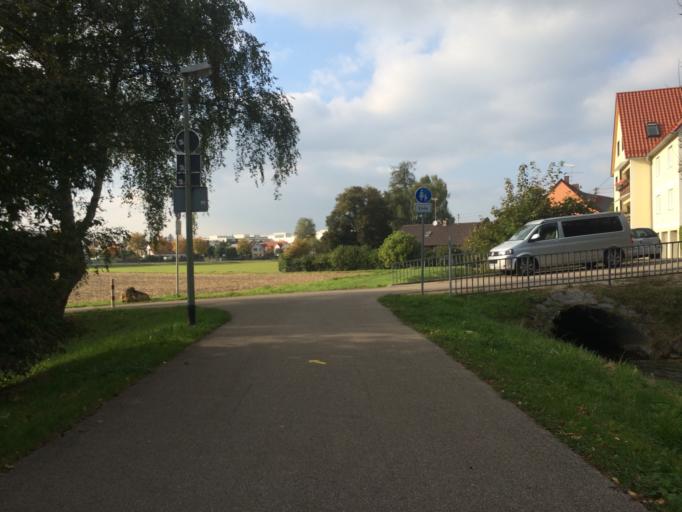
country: DE
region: Bavaria
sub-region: Swabia
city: Friedberg
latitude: 48.3531
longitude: 10.9766
